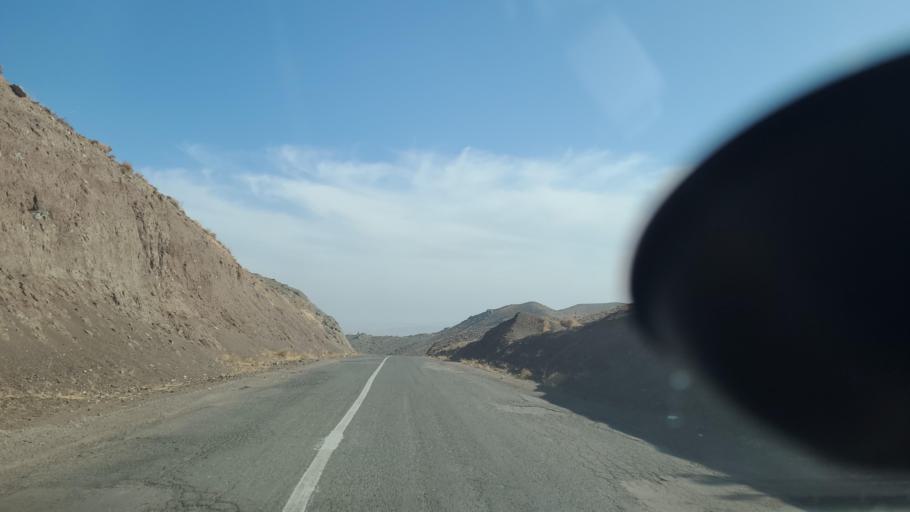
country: IR
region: Razavi Khorasan
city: Fariman
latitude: 35.5939
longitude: 59.7176
